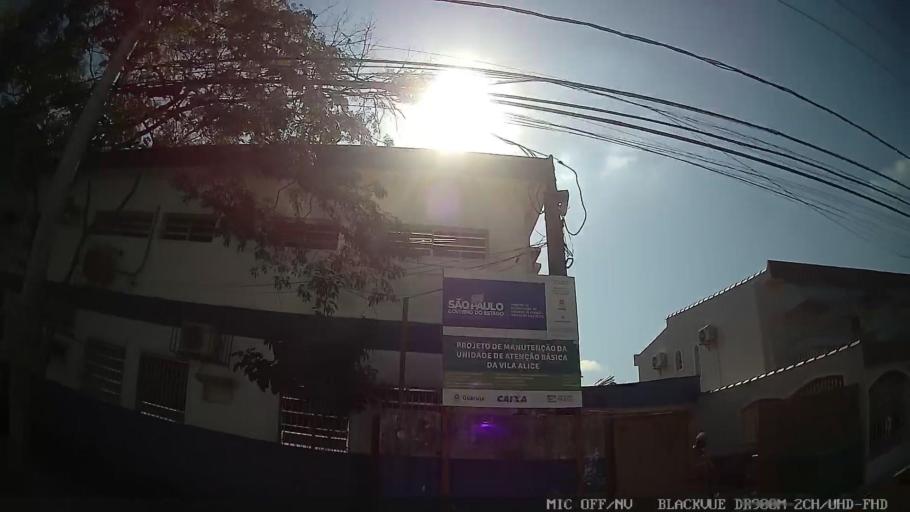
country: BR
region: Sao Paulo
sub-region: Santos
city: Santos
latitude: -23.9386
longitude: -46.3037
